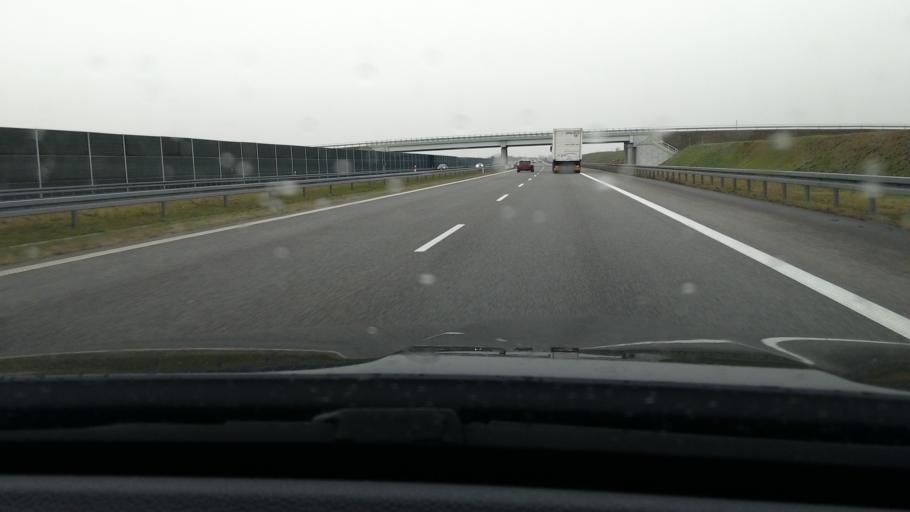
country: PL
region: Masovian Voivodeship
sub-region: Powiat warszawski zachodni
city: Bieniewice
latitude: 52.1299
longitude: 20.5417
